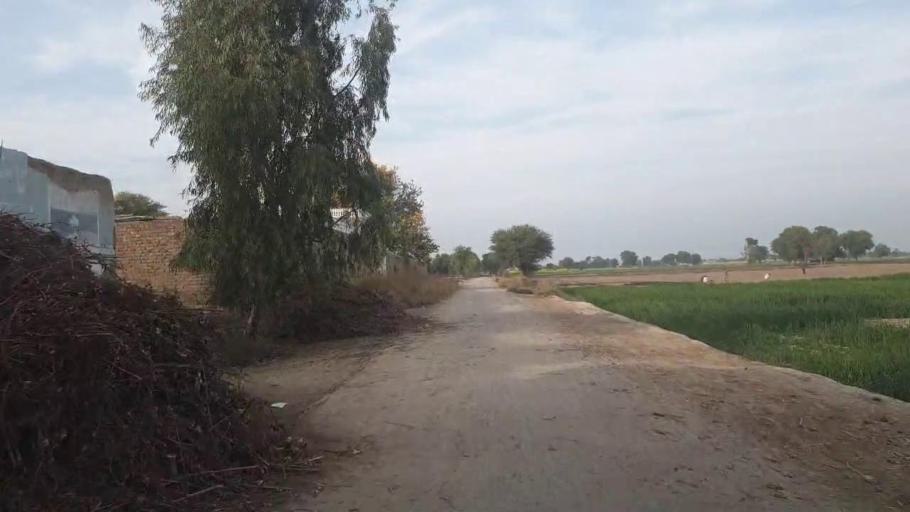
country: PK
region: Sindh
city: Shahpur Chakar
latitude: 26.1234
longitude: 68.5547
